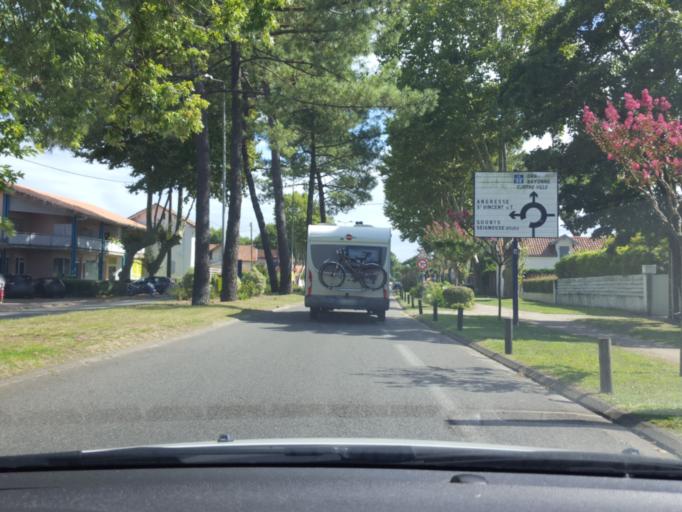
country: FR
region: Aquitaine
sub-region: Departement des Landes
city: Capbreton
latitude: 43.6448
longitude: -1.4270
